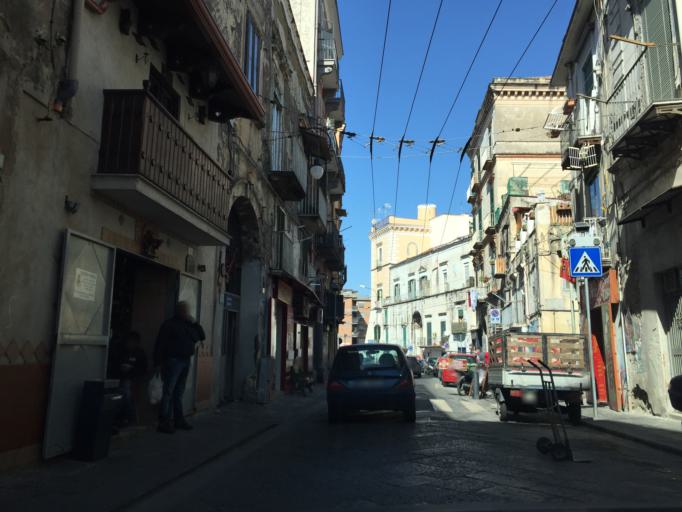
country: IT
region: Campania
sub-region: Provincia di Napoli
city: Portici
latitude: 40.8134
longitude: 14.3398
